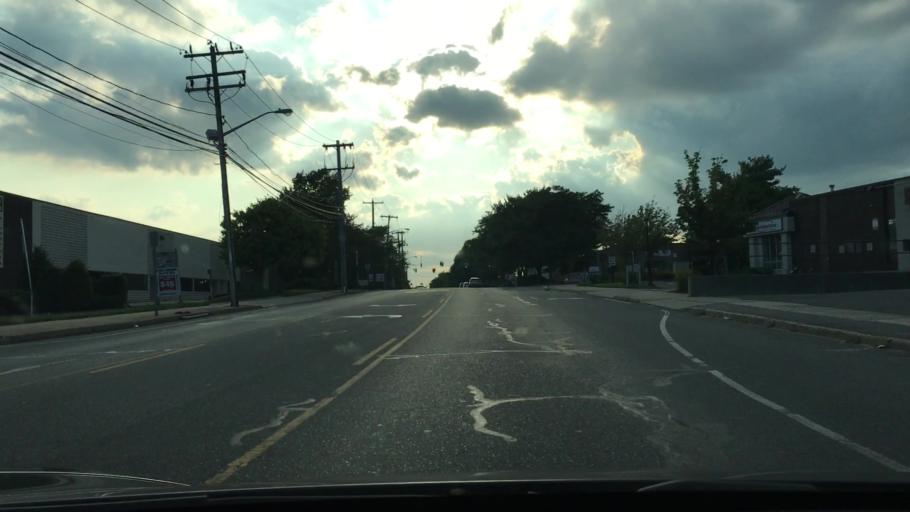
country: US
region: New York
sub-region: Suffolk County
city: Bay Wood
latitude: 40.7607
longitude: -73.2963
